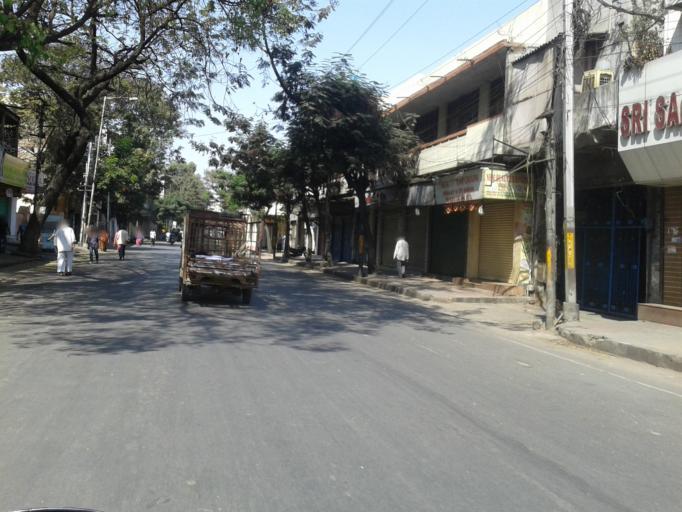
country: IN
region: Telangana
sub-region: Hyderabad
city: Hyderabad
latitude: 17.3874
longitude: 78.4861
